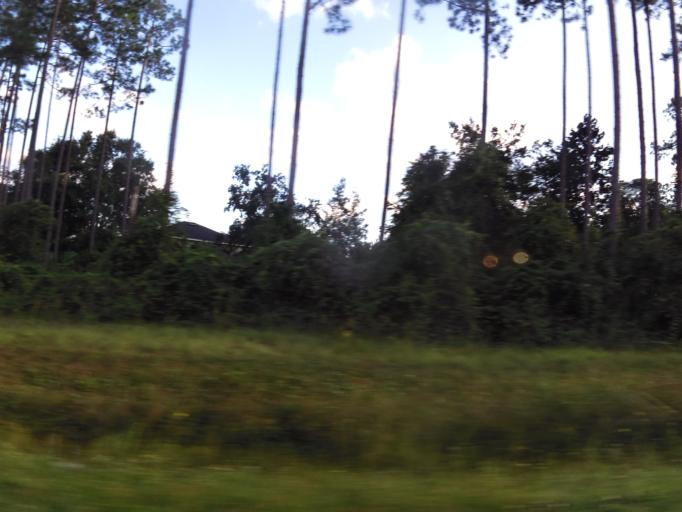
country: US
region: Florida
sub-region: Saint Johns County
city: Fruit Cove
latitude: 30.0559
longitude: -81.5458
